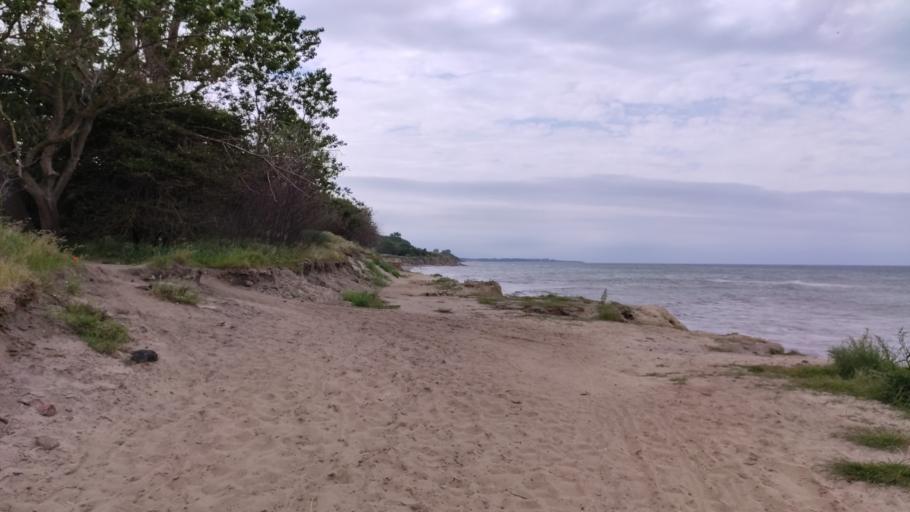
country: DE
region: Mecklenburg-Vorpommern
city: Bastorf
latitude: 54.1401
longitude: 11.6605
